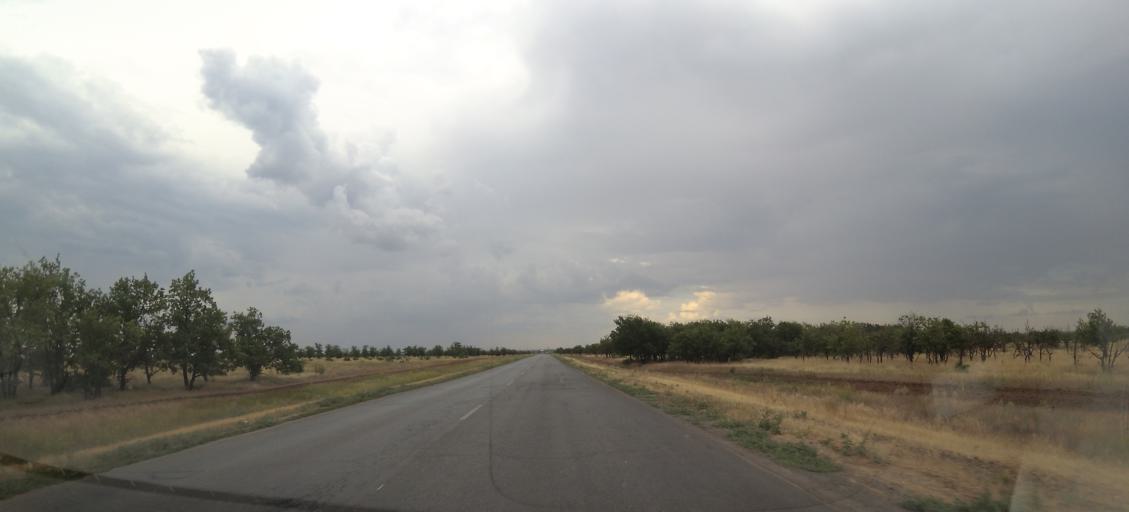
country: RU
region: Volgograd
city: Kotel'nikovo
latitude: 47.6118
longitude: 43.1134
